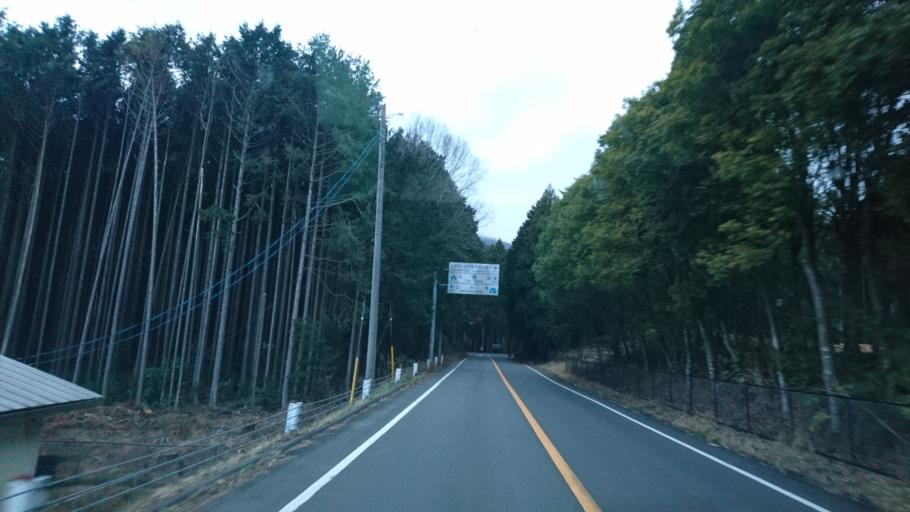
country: JP
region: Shizuoka
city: Fujinomiya
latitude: 35.3334
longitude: 138.5766
